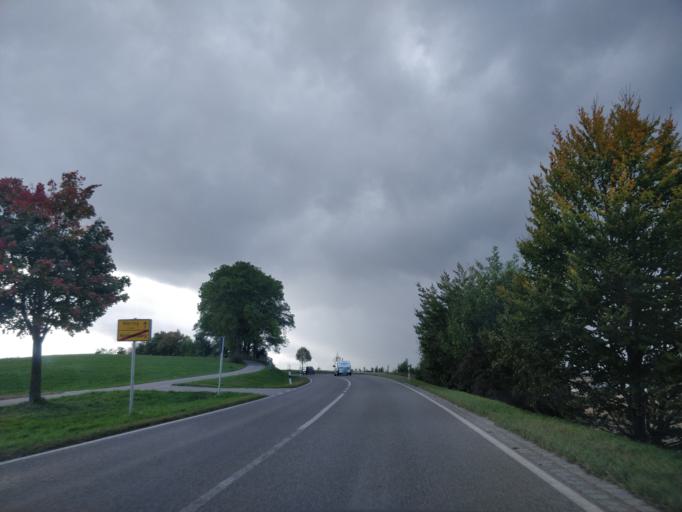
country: DE
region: Bavaria
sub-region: Swabia
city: Ried
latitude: 48.2830
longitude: 11.0190
